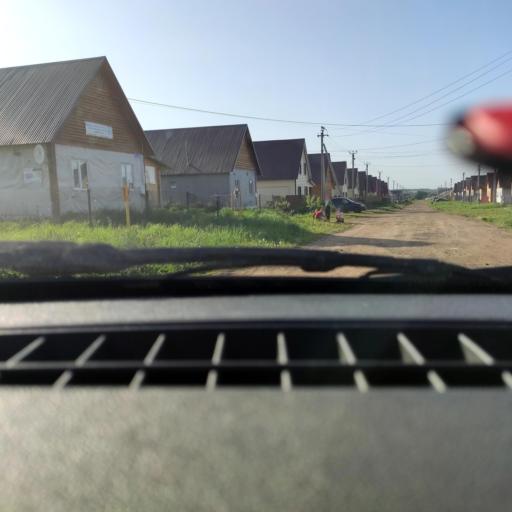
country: RU
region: Bashkortostan
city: Iglino
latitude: 54.8177
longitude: 56.4390
